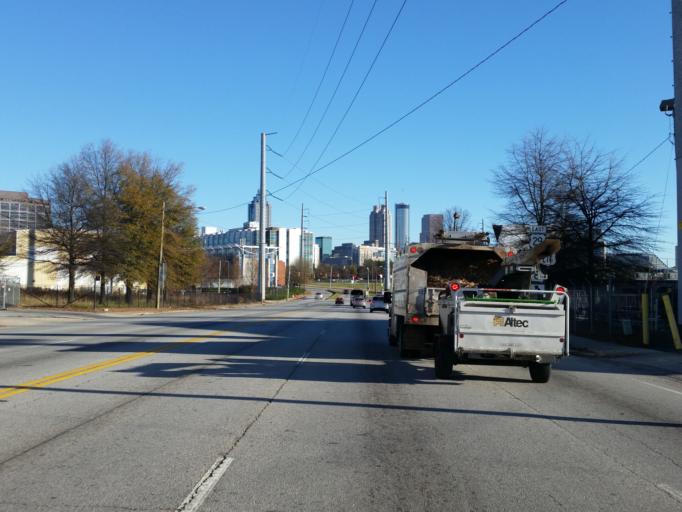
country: US
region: Georgia
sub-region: Fulton County
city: Atlanta
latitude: 33.7714
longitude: -84.4064
